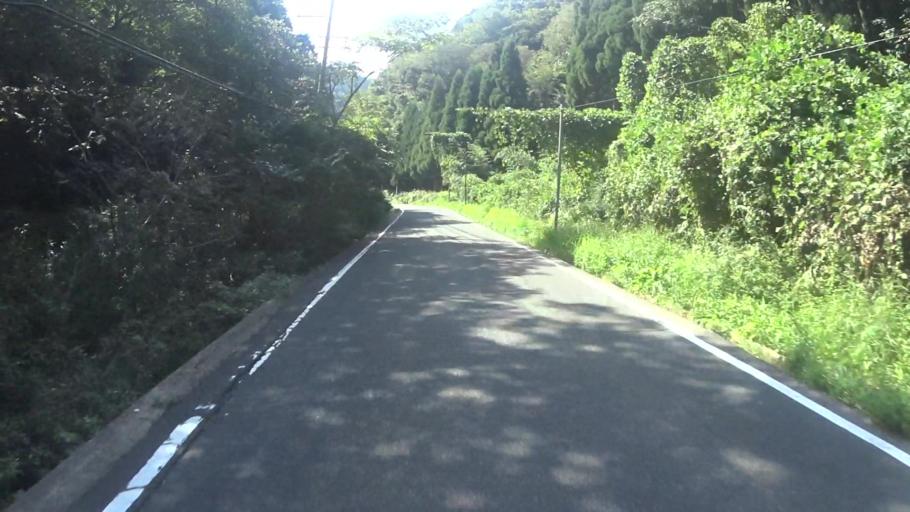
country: JP
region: Kyoto
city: Miyazu
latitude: 35.6875
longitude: 135.2875
